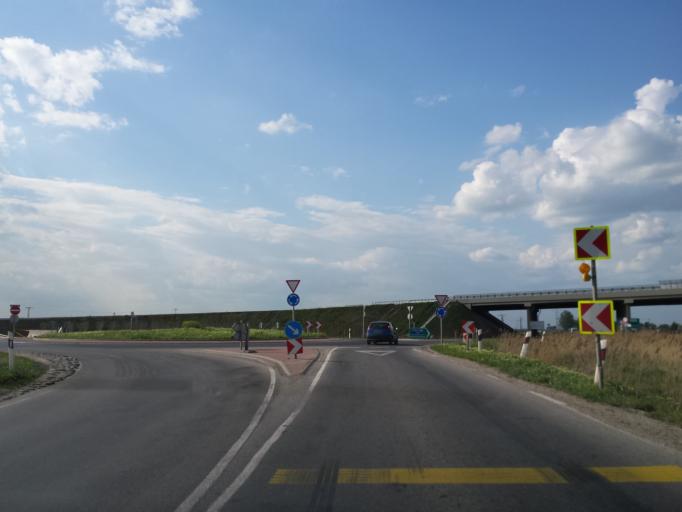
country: HU
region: Csongrad
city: Mako
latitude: 46.2662
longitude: 20.4820
